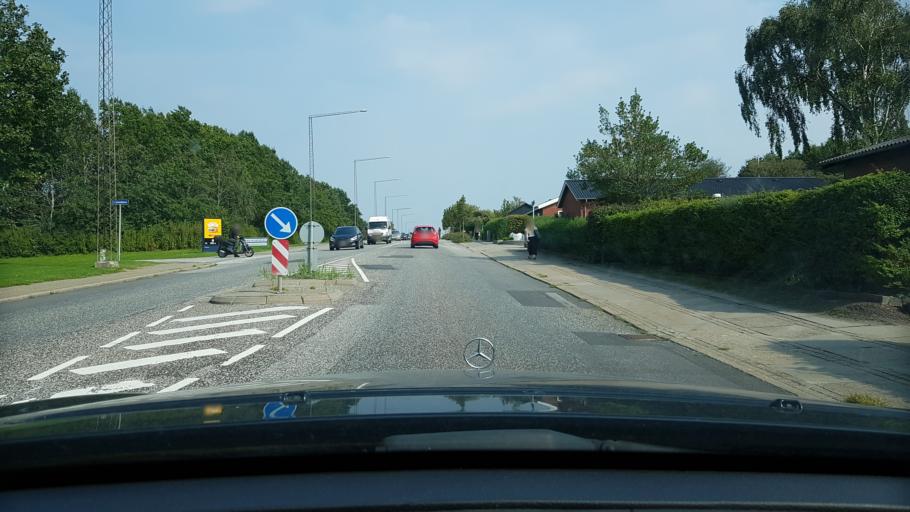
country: DK
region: North Denmark
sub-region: Alborg Kommune
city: Aalborg
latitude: 57.0706
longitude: 9.9263
